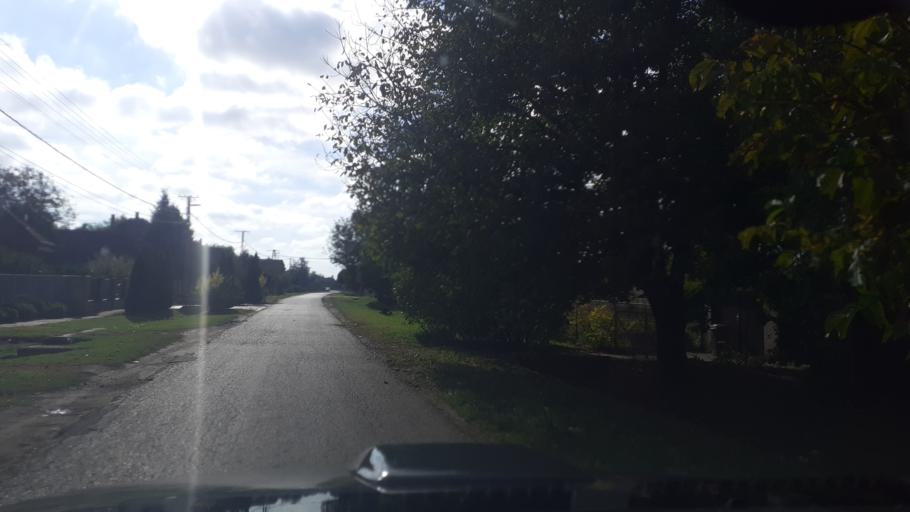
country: HU
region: Fejer
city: Baracs
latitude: 46.9207
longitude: 18.8776
